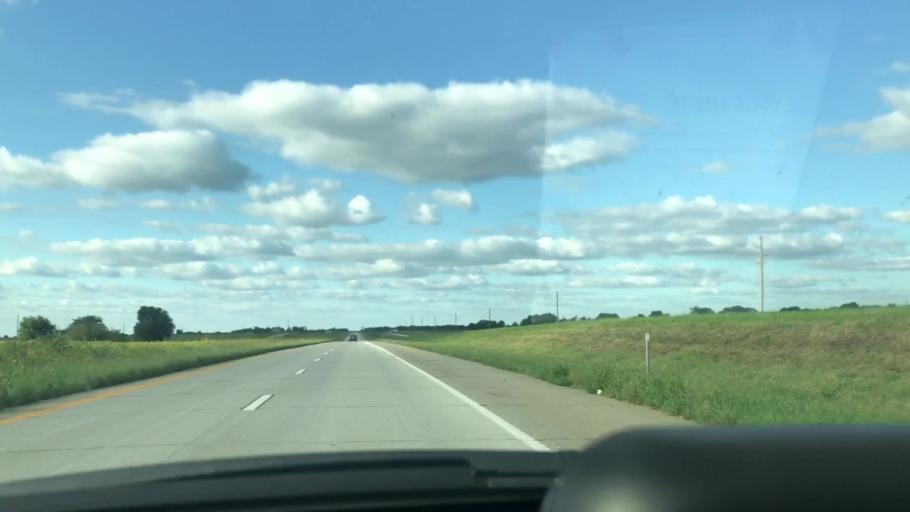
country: US
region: Missouri
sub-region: Benton County
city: Cole Camp
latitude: 38.5085
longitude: -93.2728
